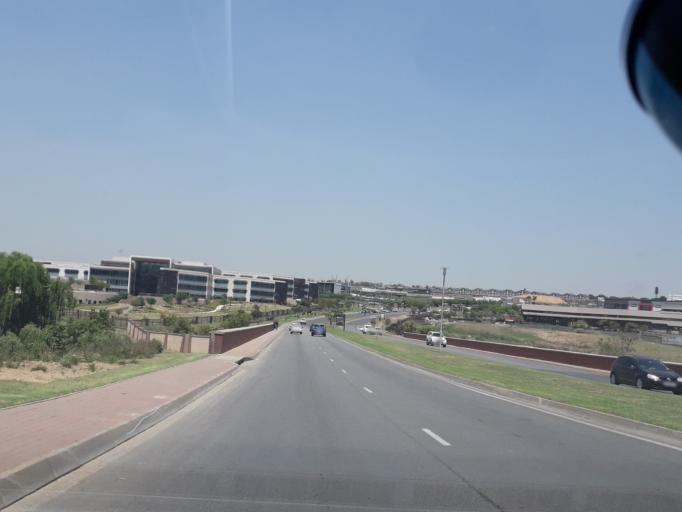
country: ZA
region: Gauteng
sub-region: City of Johannesburg Metropolitan Municipality
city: Midrand
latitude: -26.0172
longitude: 28.0923
